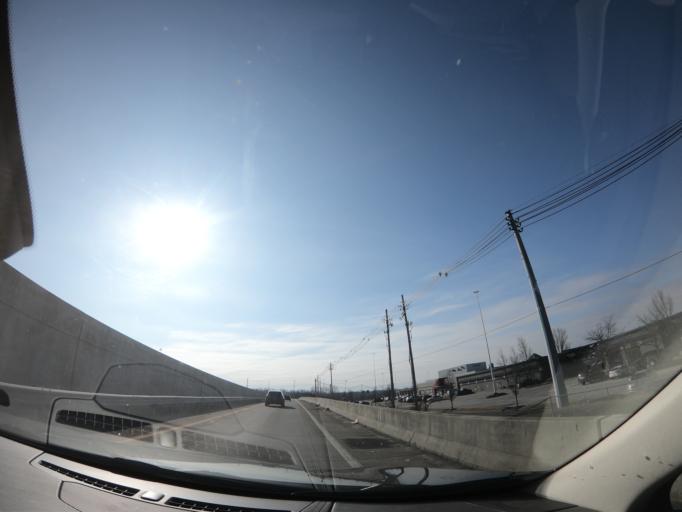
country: US
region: Kentucky
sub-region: Jefferson County
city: Beechwood Village
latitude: 38.2490
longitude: -85.6214
